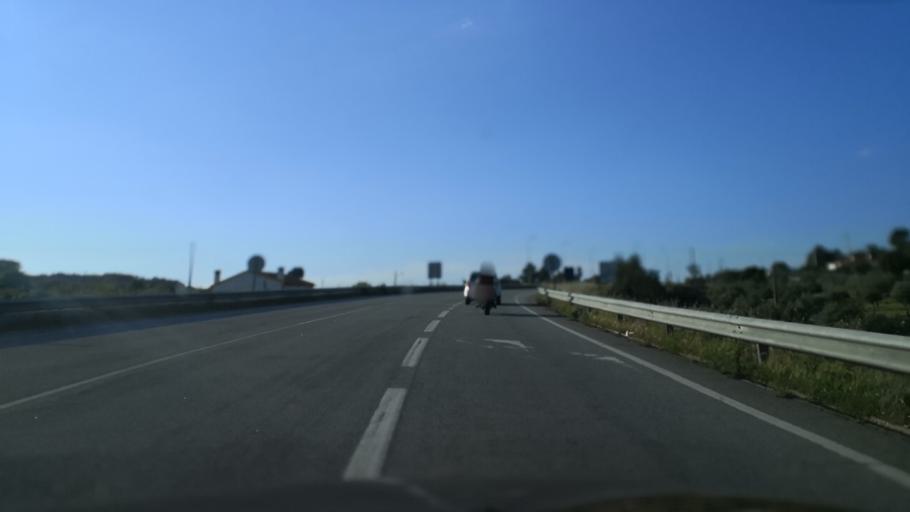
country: PT
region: Portalegre
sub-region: Portalegre
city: Portalegre
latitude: 39.3083
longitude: -7.4429
